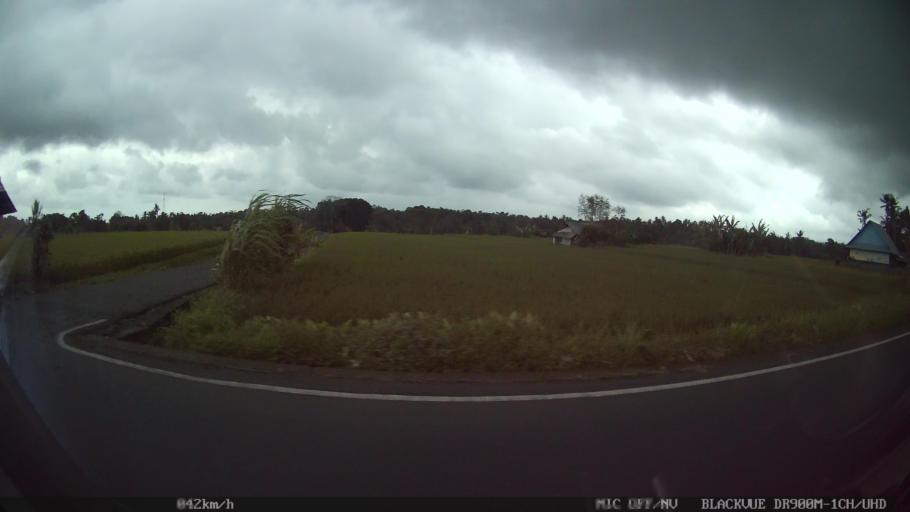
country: ID
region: Bali
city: Banjar Keraman
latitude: -8.5322
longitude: 115.2256
